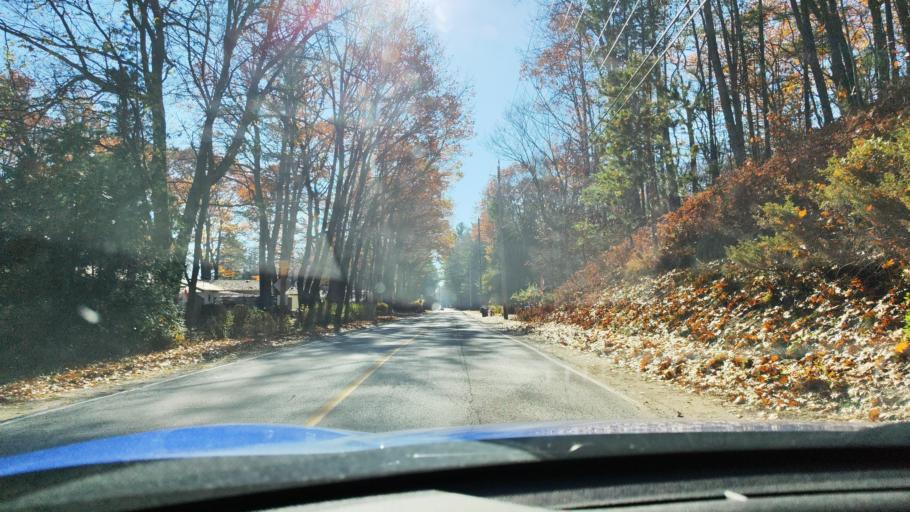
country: CA
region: Ontario
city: Wasaga Beach
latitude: 44.4958
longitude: -80.0036
